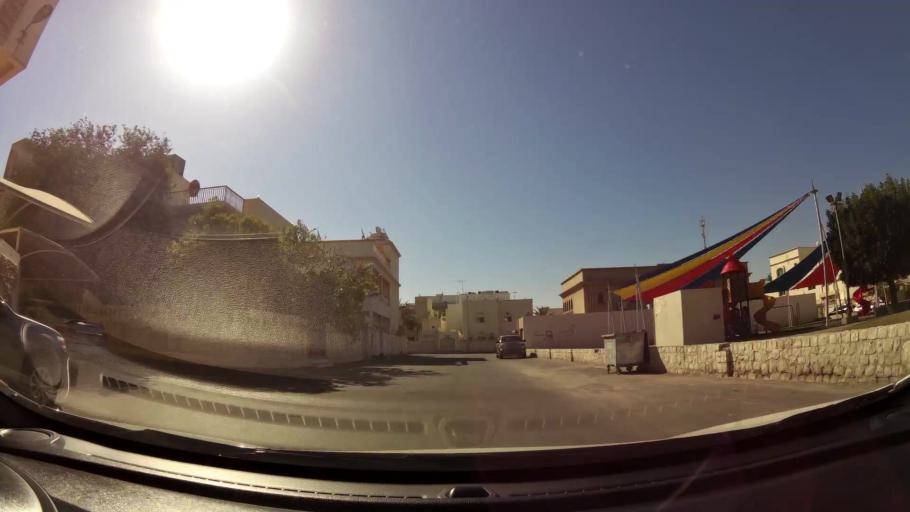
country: BH
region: Muharraq
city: Al Muharraq
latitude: 26.2607
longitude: 50.6209
